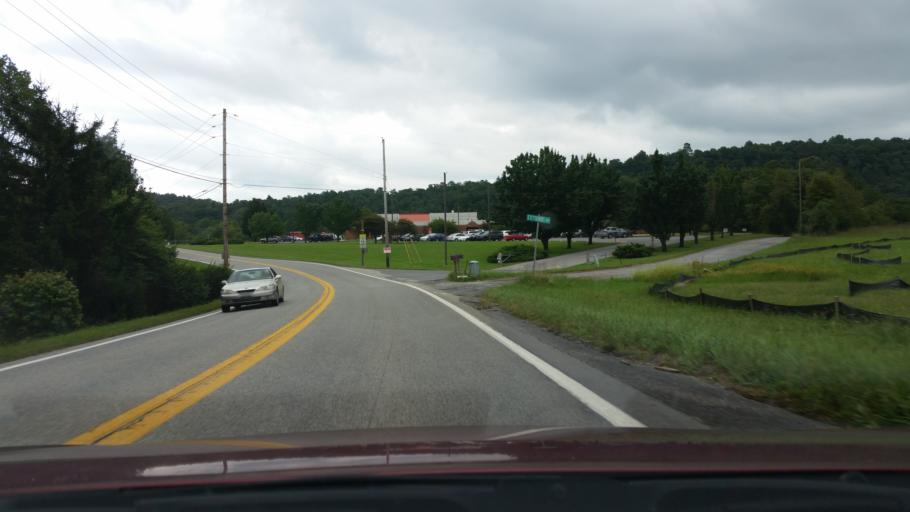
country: US
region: West Virginia
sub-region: Berkeley County
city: Martinsburg
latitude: 39.5541
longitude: -78.0236
